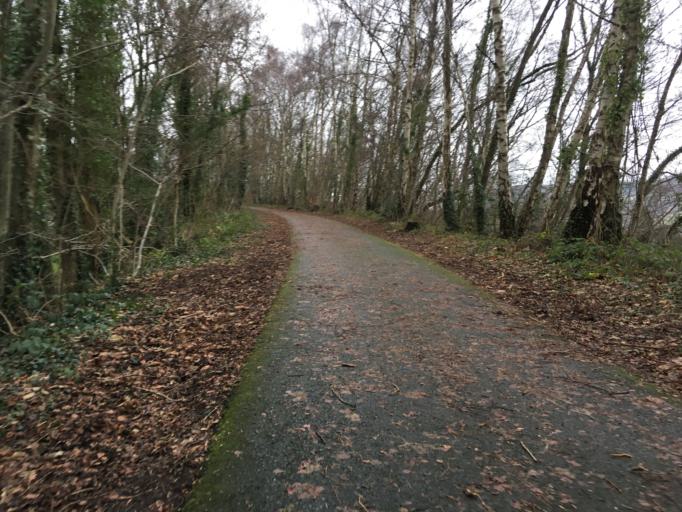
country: GB
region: Wales
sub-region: Monmouthshire
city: Abergavenny
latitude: 51.8184
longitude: -3.0437
